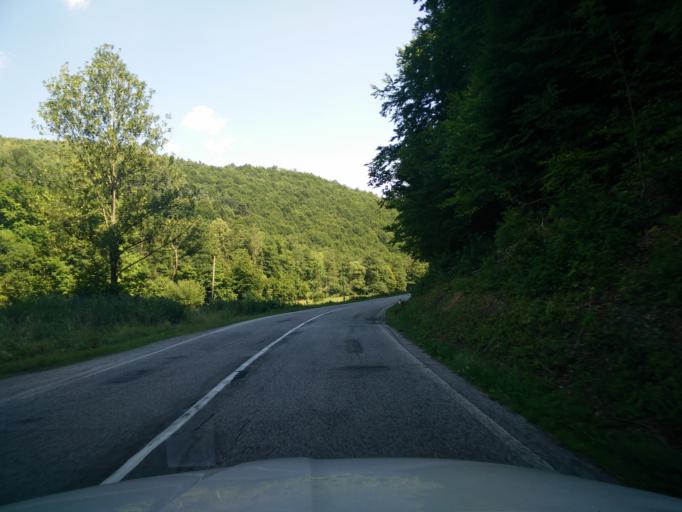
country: SK
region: Nitriansky
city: Bojnice
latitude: 48.8637
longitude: 18.4579
